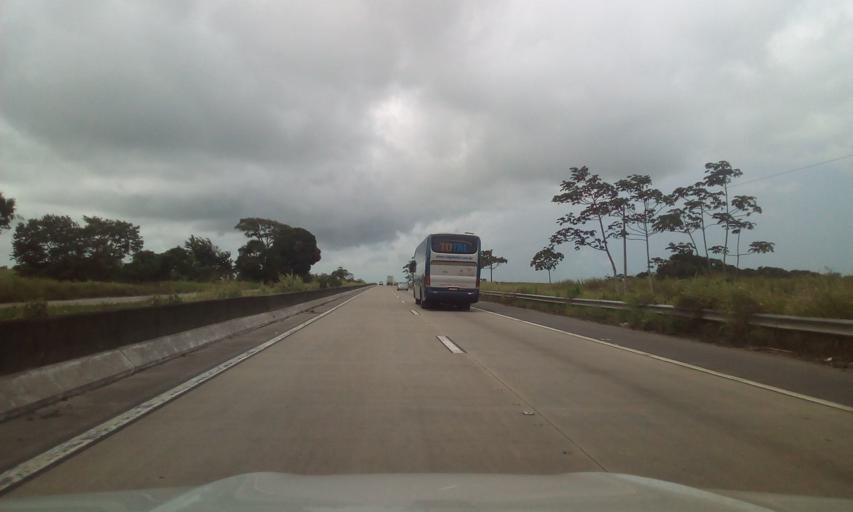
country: BR
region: Pernambuco
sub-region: Itapissuma
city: Itapissuma
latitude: -7.7157
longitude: -34.9360
